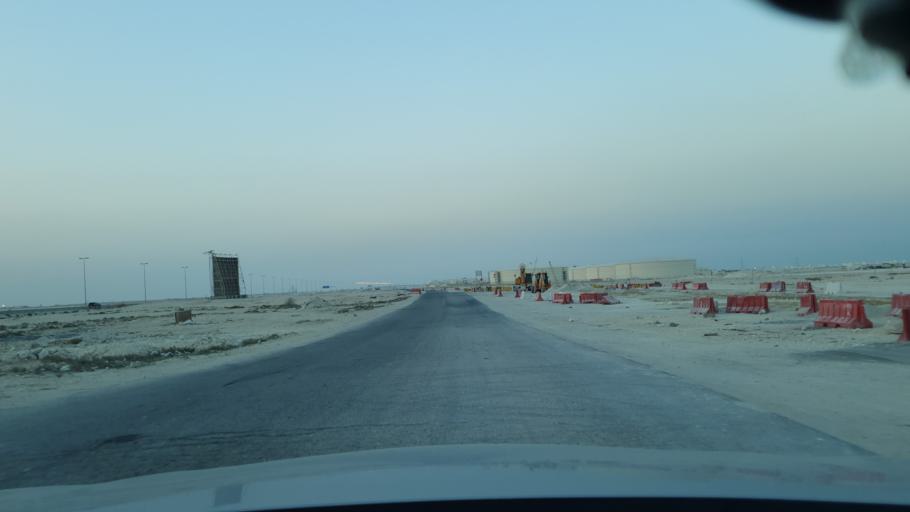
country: BH
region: Central Governorate
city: Dar Kulayb
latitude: 25.9708
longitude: 50.6019
